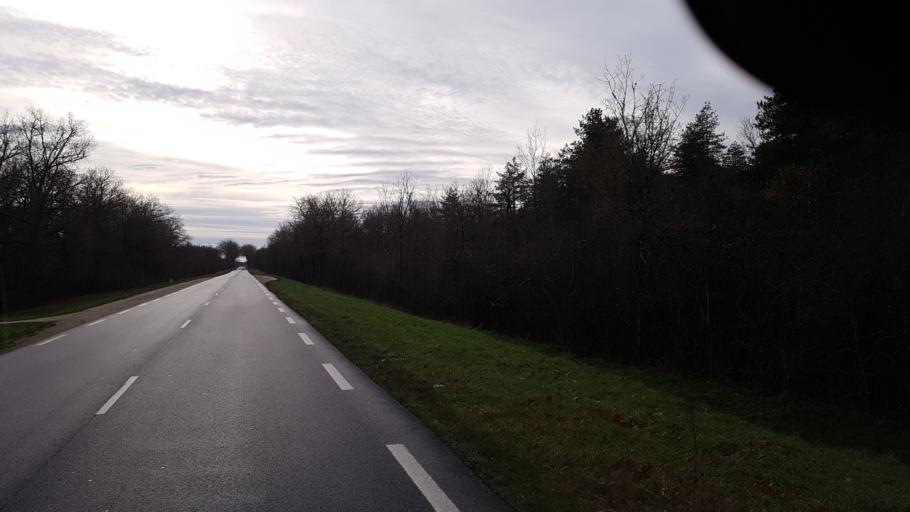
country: FR
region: Centre
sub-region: Departement du Loiret
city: Saint-Cyr-en-Val
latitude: 47.7827
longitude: 1.9349
